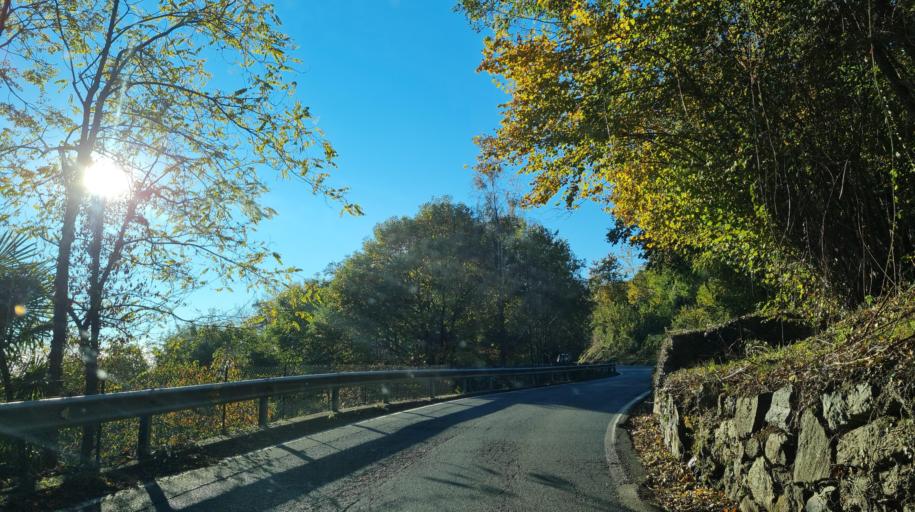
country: IT
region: Piedmont
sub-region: Provincia di Torino
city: Lessolo
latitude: 45.4727
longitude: 7.8069
